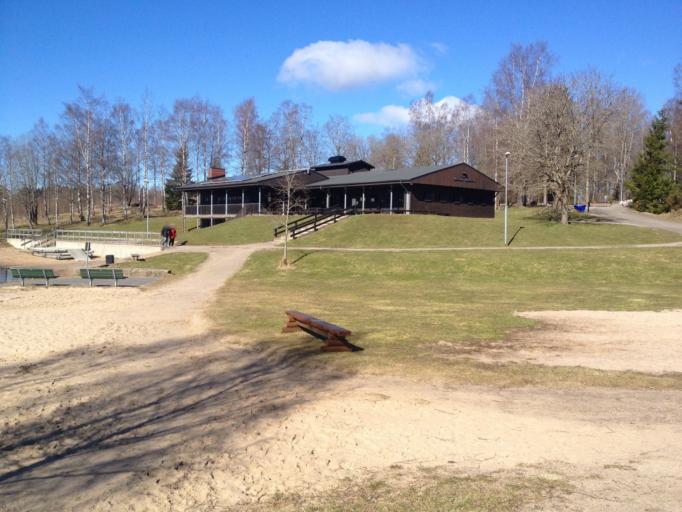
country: SE
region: Vaestra Goetaland
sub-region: Falkopings Kommun
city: Falkoeping
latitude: 58.1746
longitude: 13.5232
